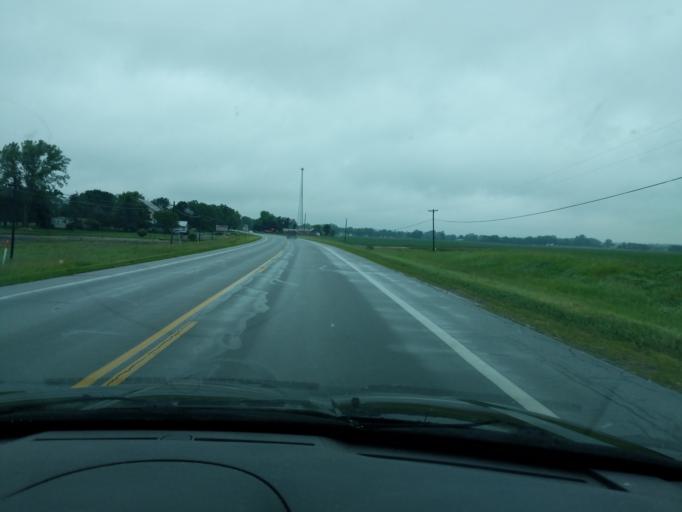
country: US
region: Ohio
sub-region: Logan County
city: West Liberty
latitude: 40.2365
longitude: -83.7517
